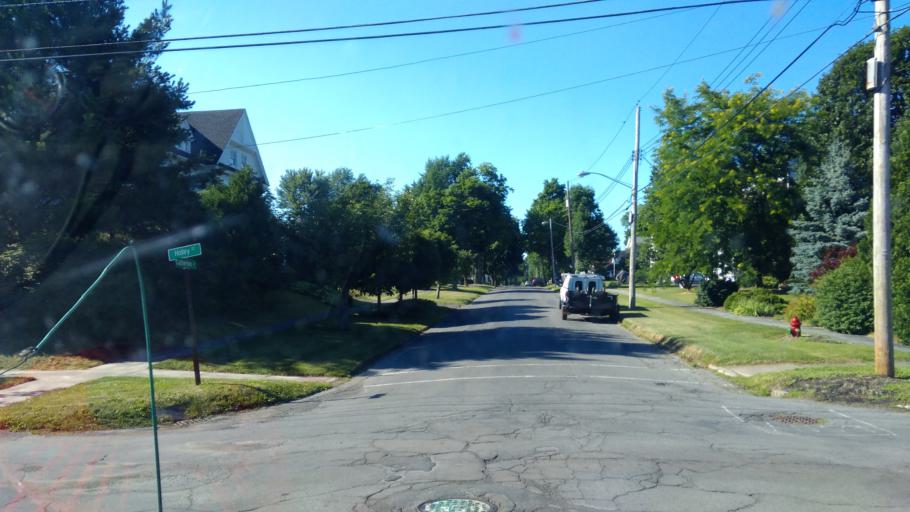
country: US
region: New York
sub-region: Wayne County
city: Lyons
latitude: 43.0671
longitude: -76.9875
